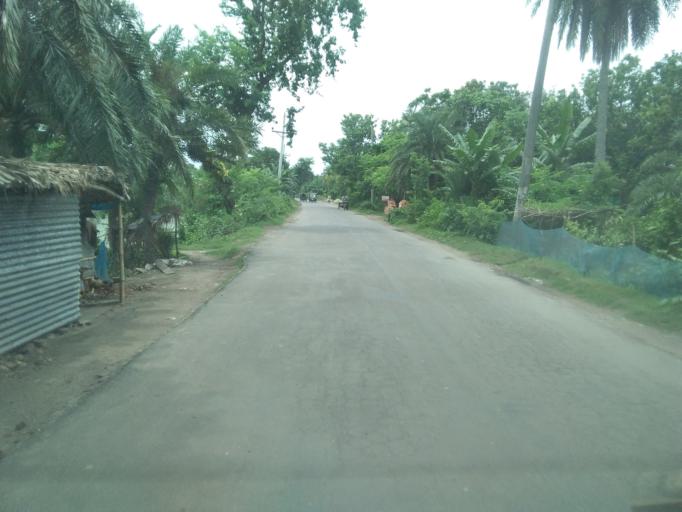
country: IN
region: West Bengal
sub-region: North 24 Parganas
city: Taki
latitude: 22.5798
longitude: 88.9983
